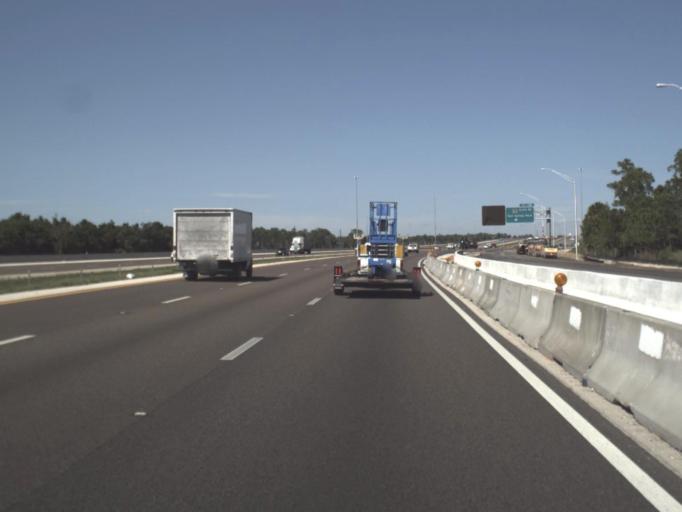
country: US
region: Florida
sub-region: Lee County
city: Three Oaks
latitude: 26.4829
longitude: -81.7936
